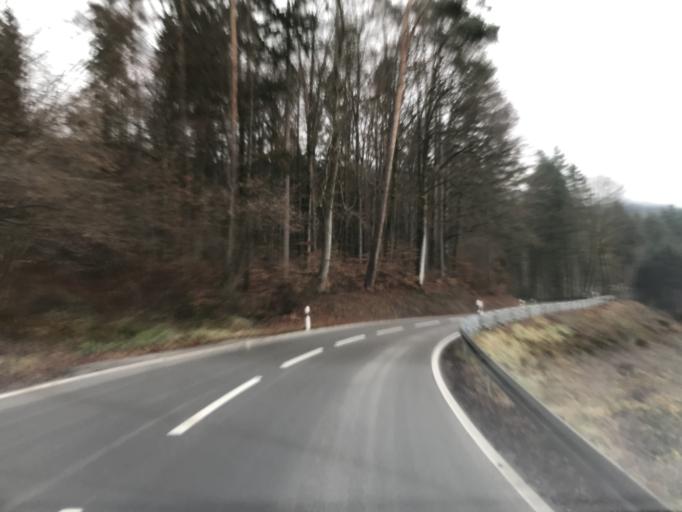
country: DE
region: Baden-Wuerttemberg
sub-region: Freiburg Region
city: Wehr
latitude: 47.6236
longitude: 7.9216
